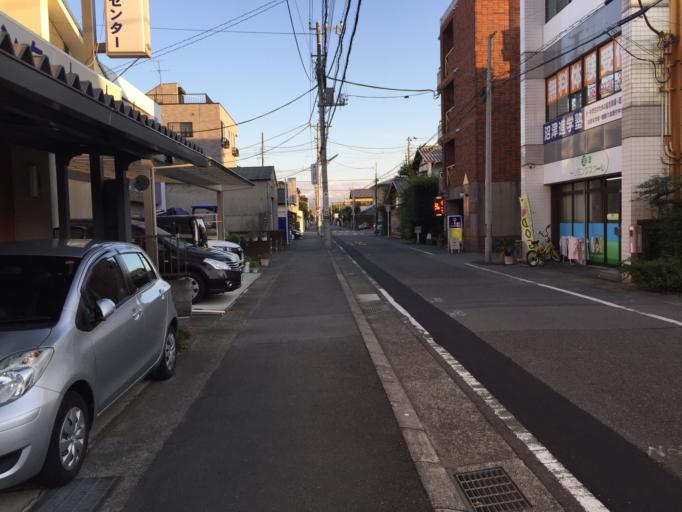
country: JP
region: Shizuoka
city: Numazu
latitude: 35.0940
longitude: 138.8632
